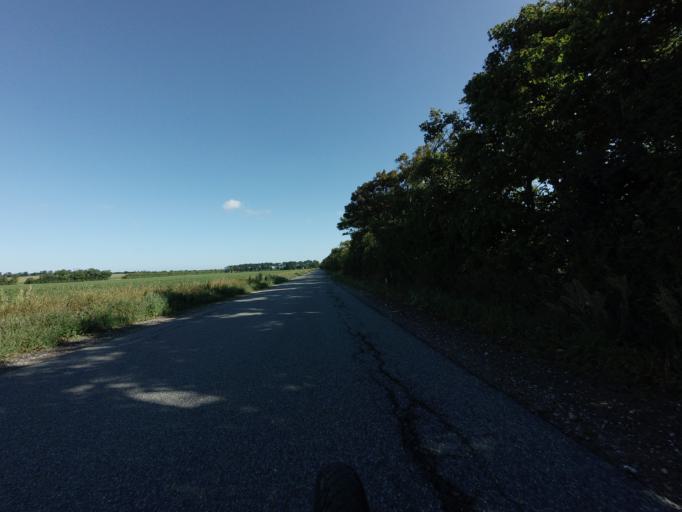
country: DK
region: North Denmark
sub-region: Hjorring Kommune
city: Vra
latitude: 57.3668
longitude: 10.0034
